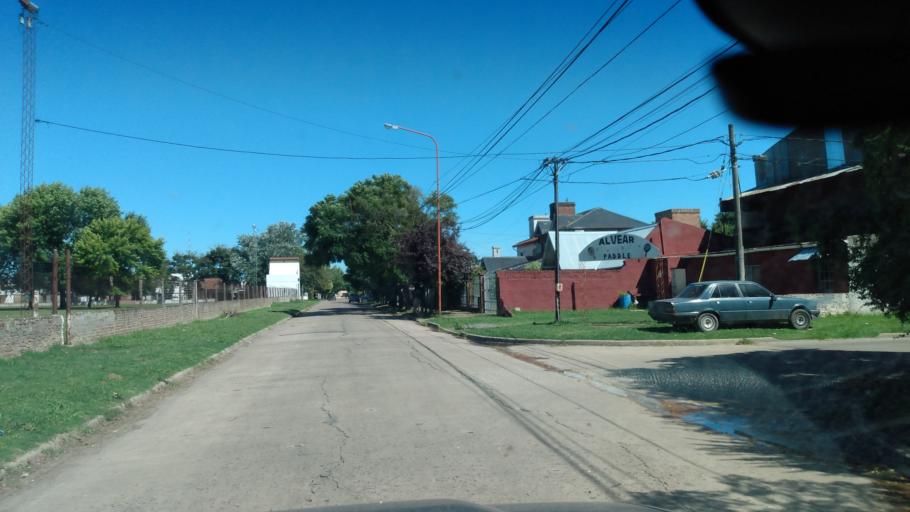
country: AR
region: Buenos Aires
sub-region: Partido de Lujan
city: Lujan
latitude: -34.5773
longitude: -59.1095
